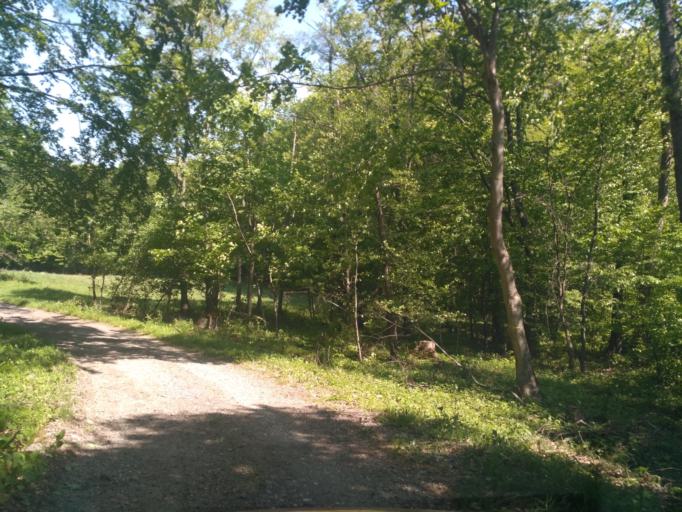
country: SK
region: Presovsky
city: Vranov nad Topl'ou
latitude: 48.8392
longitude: 21.4816
